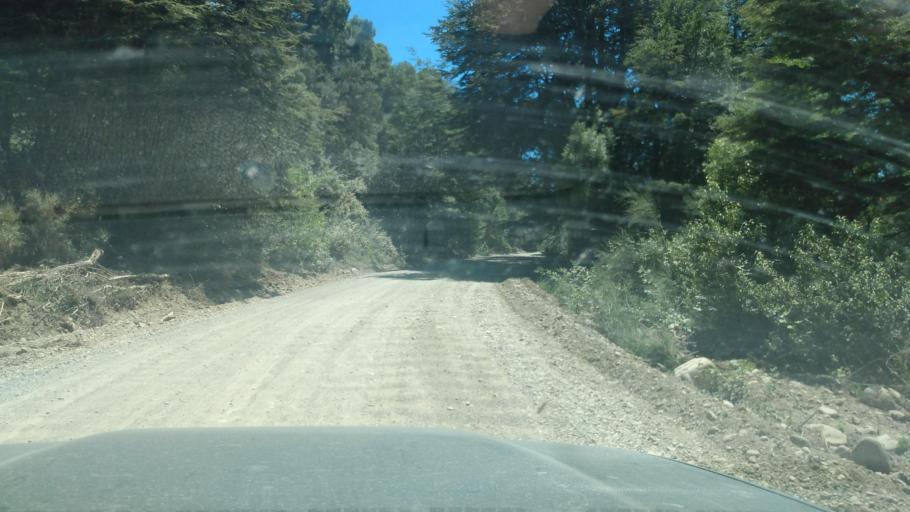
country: AR
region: Rio Negro
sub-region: Departamento de Bariloche
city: San Carlos de Bariloche
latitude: -41.1299
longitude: -71.4529
